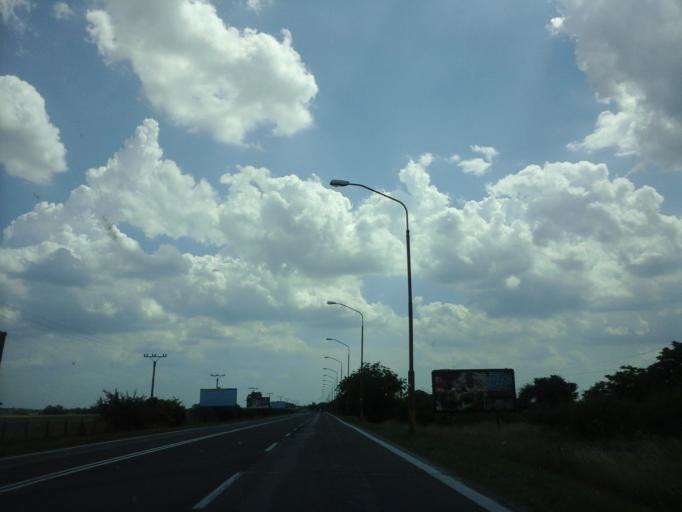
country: HU
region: Gyor-Moson-Sopron
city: Rajka
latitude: 48.0312
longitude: 17.1667
